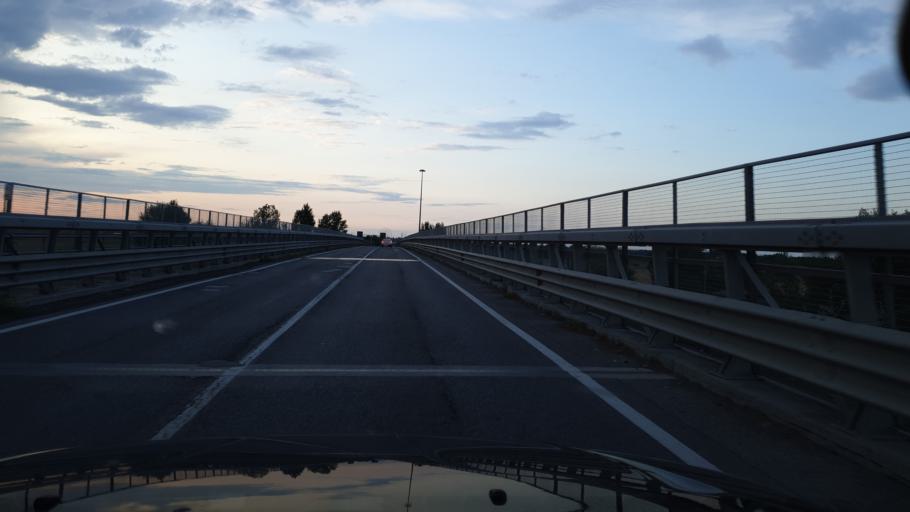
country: IT
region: Emilia-Romagna
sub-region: Provincia di Ravenna
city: Savio
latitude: 44.3025
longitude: 12.2907
